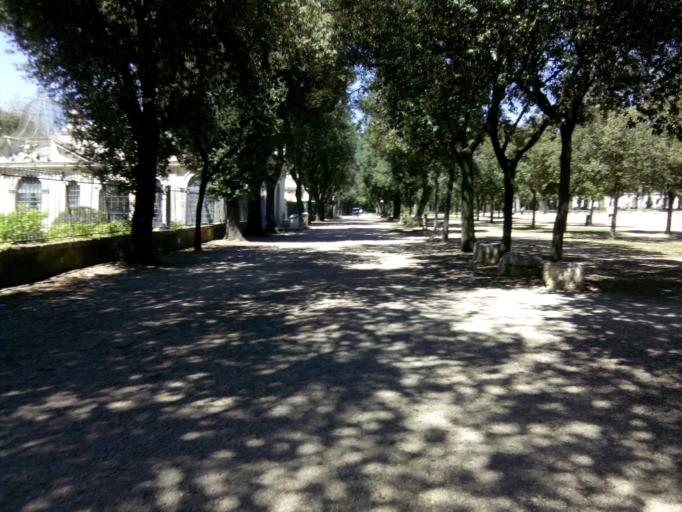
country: IT
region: Latium
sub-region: Citta metropolitana di Roma Capitale
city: Rome
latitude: 41.9148
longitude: 12.4918
